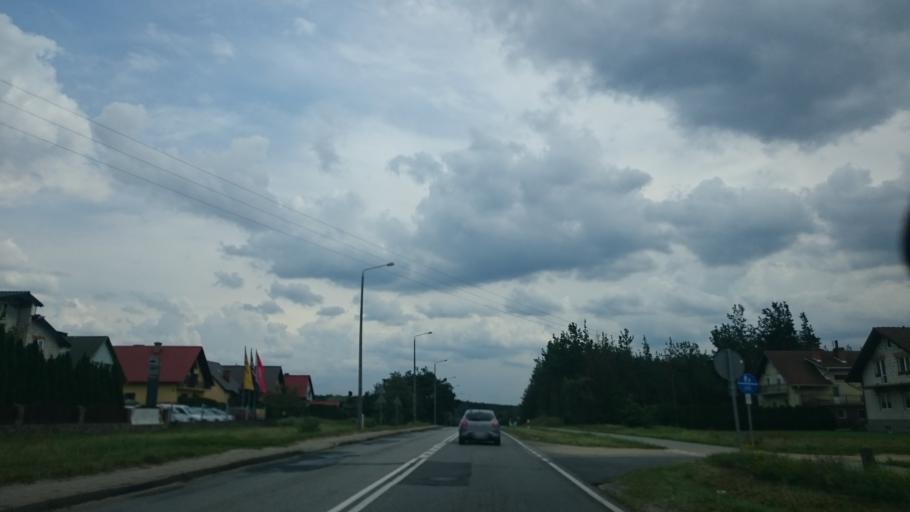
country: PL
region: Kujawsko-Pomorskie
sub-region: Powiat tucholski
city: Tuchola
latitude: 53.5688
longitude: 17.8916
